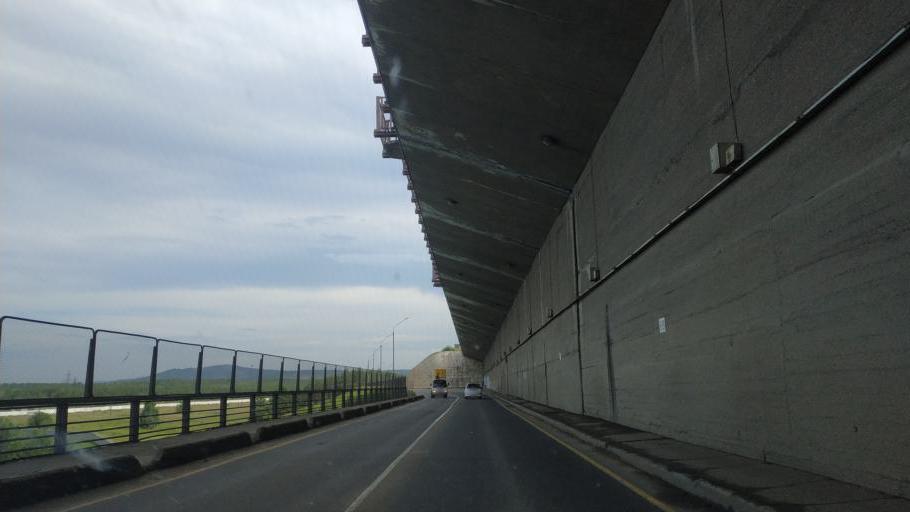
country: RU
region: Irkutsk
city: Bratsk
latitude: 56.2831
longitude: 101.7891
